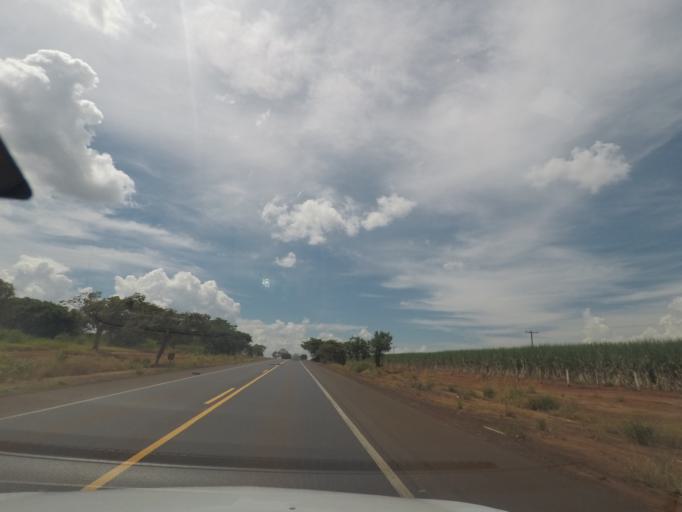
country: BR
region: Sao Paulo
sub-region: Barretos
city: Barretos
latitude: -20.2833
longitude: -48.6708
